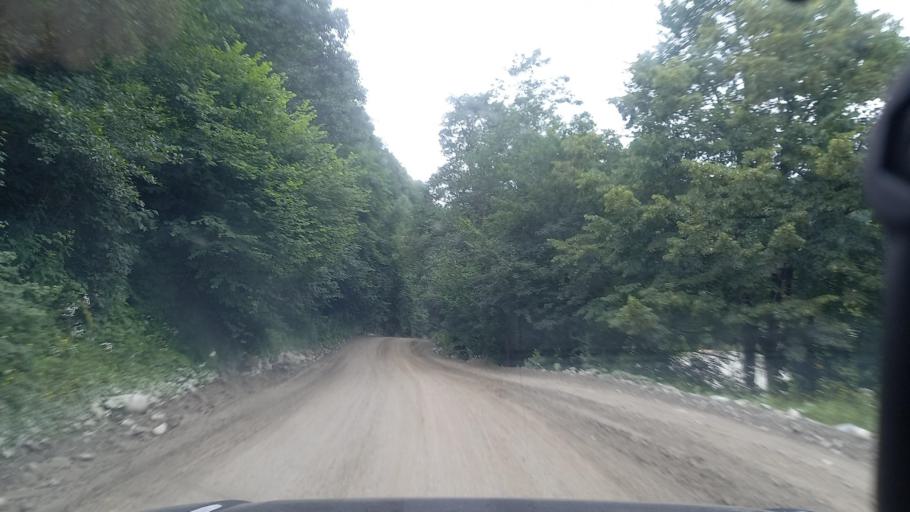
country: RU
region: Karachayevo-Cherkesiya
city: Kurdzhinovo
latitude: 43.9465
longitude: 40.9603
